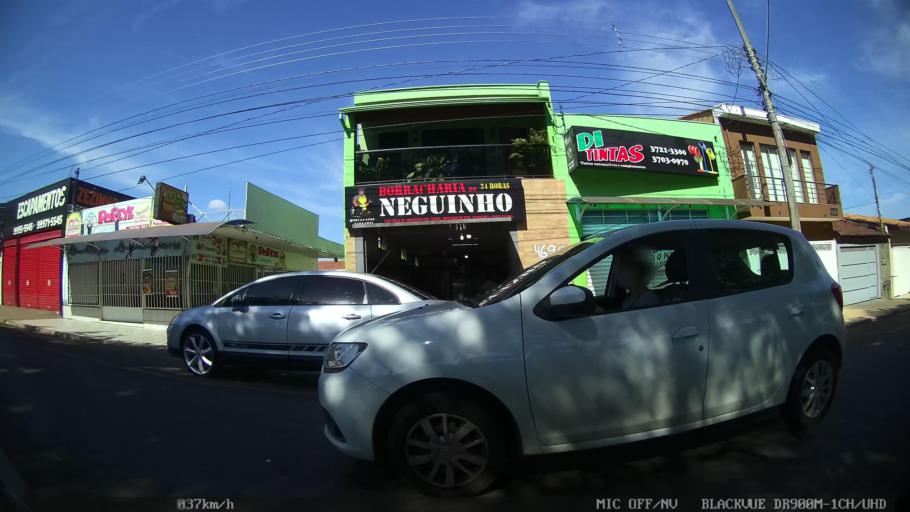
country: BR
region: Sao Paulo
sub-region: Franca
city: Franca
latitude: -20.5119
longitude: -47.4025
